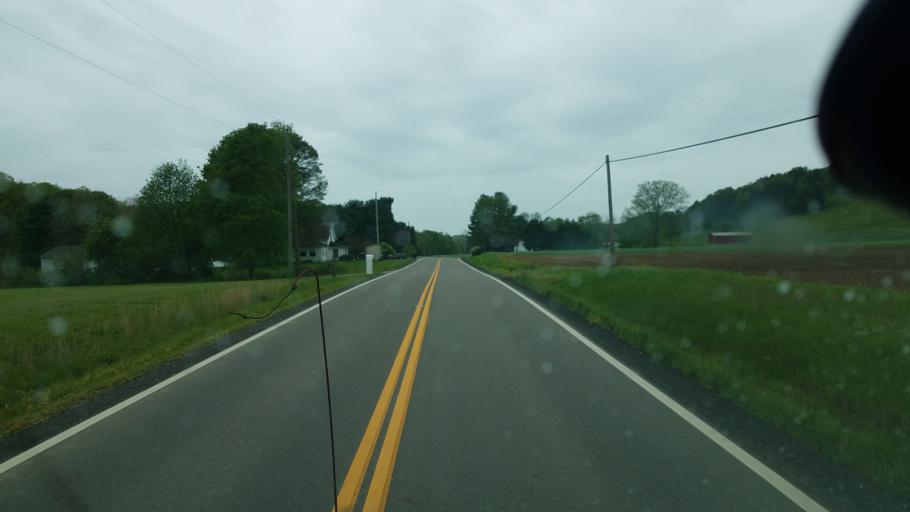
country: US
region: Ohio
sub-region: Coshocton County
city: West Lafayette
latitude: 40.2199
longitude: -81.7590
